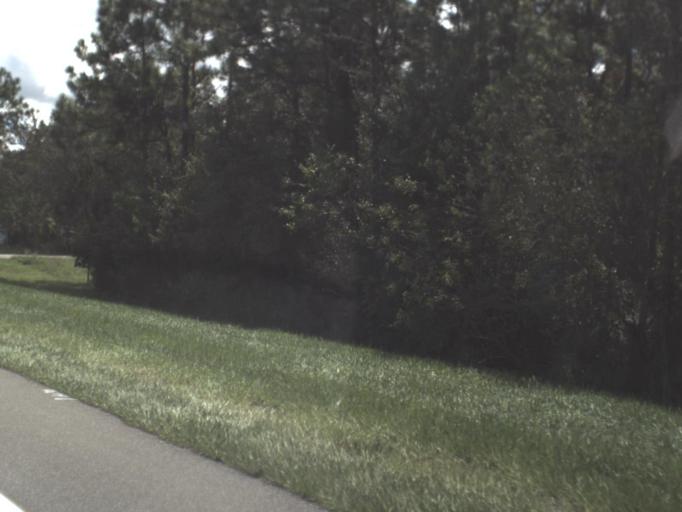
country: US
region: Florida
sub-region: Sarasota County
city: The Meadows
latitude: 27.4179
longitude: -82.3597
